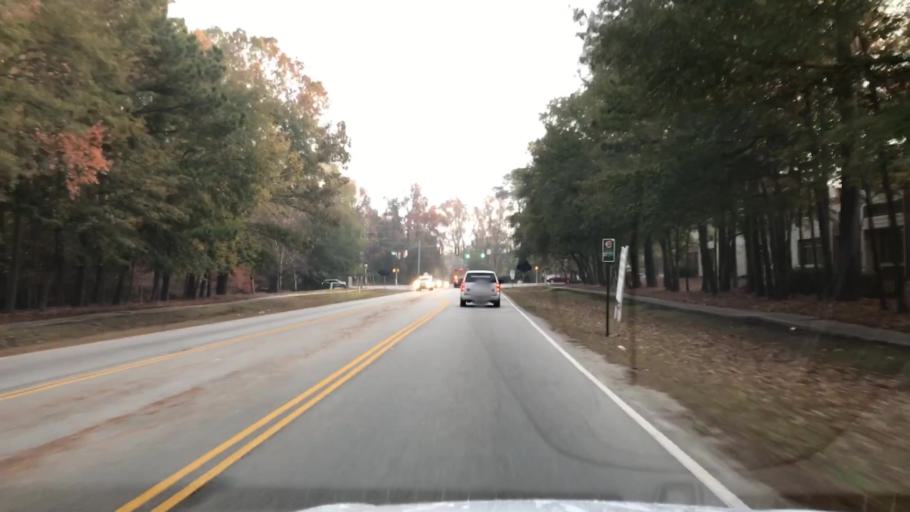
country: US
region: South Carolina
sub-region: Charleston County
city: North Charleston
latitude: 32.8104
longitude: -80.0293
